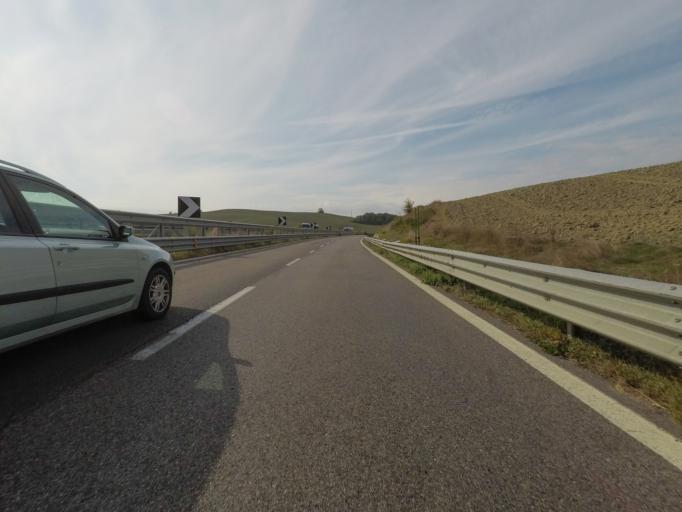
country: IT
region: Tuscany
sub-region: Provincia di Siena
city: Isola D'Arbia
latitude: 43.2577
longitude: 11.3255
